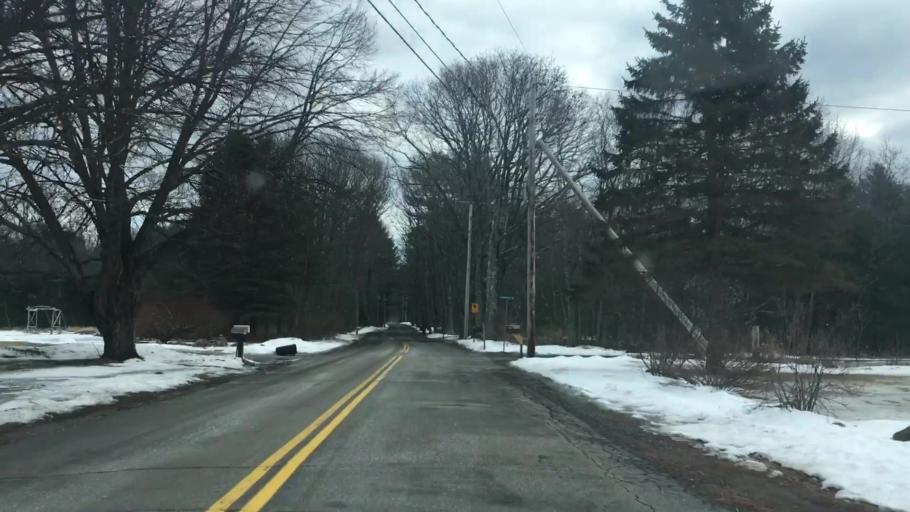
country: US
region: Maine
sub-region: York County
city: Wells Beach Station
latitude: 43.3434
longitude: -70.6153
